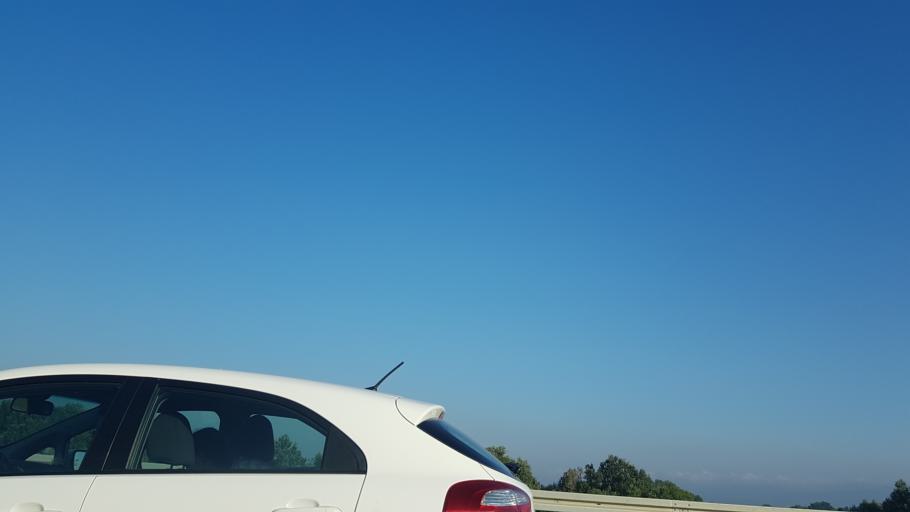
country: TR
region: Bursa
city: Karacabey
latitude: 40.1825
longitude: 28.3313
